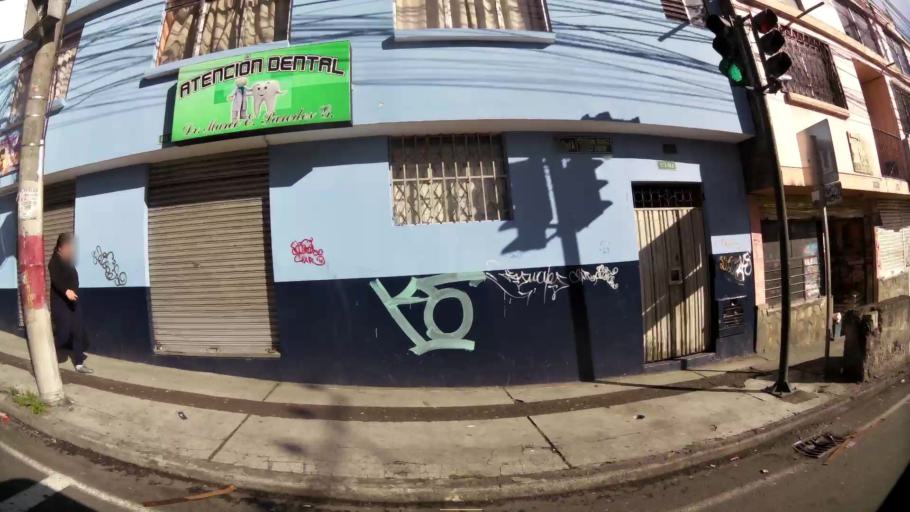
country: EC
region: Pichincha
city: Quito
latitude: -0.2630
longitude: -78.5263
